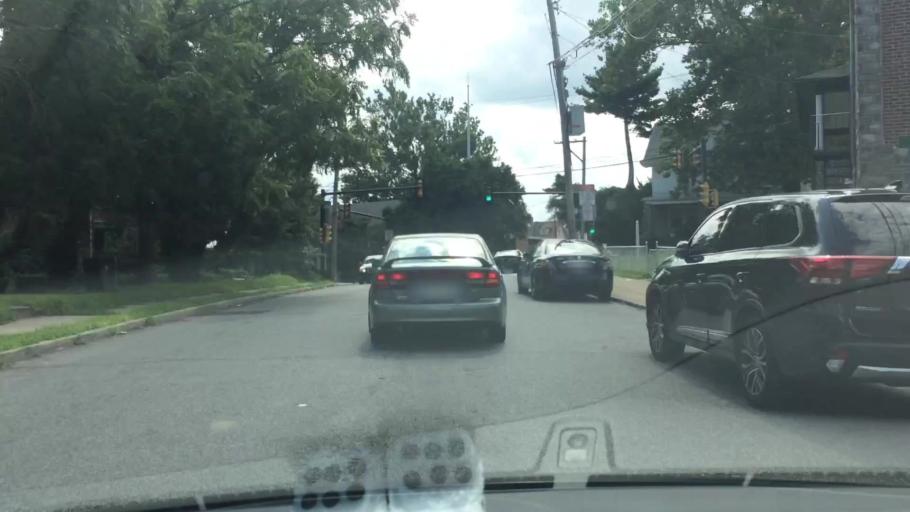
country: US
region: Pennsylvania
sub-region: Delaware County
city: Yeadon
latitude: 39.9289
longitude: -75.2462
